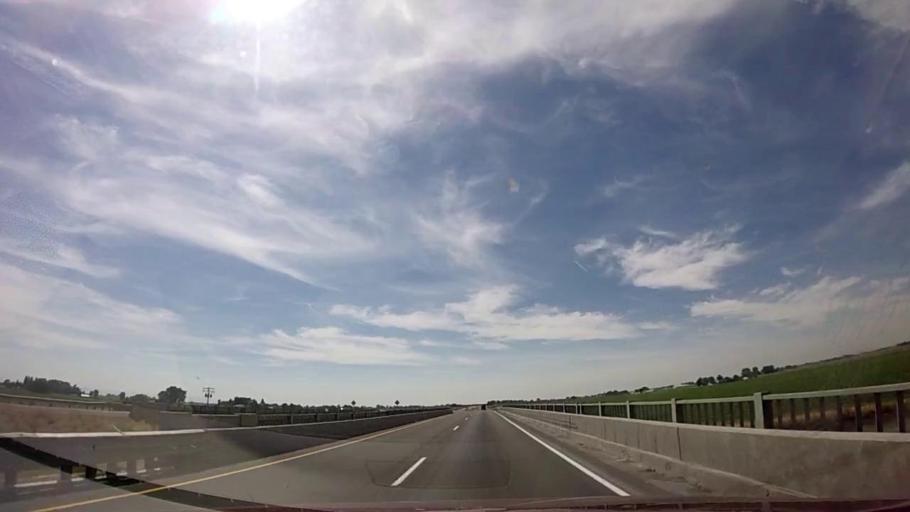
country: US
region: Idaho
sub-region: Minidoka County
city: Rupert
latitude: 42.5690
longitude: -113.6630
